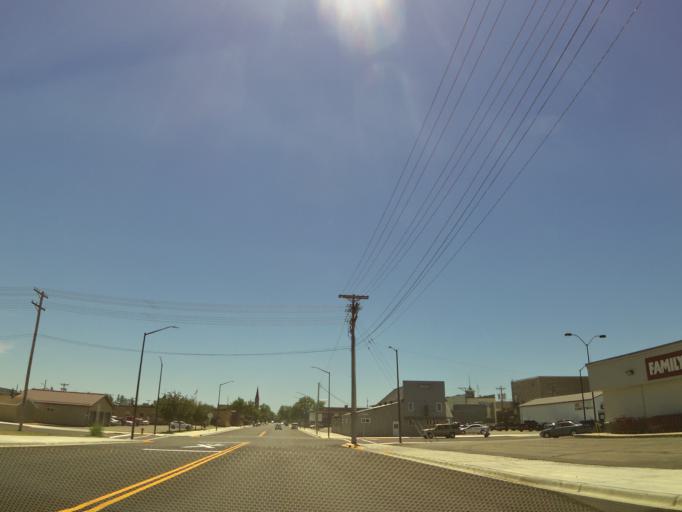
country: US
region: Minnesota
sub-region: Wadena County
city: Wadena
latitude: 46.4411
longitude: -95.1352
